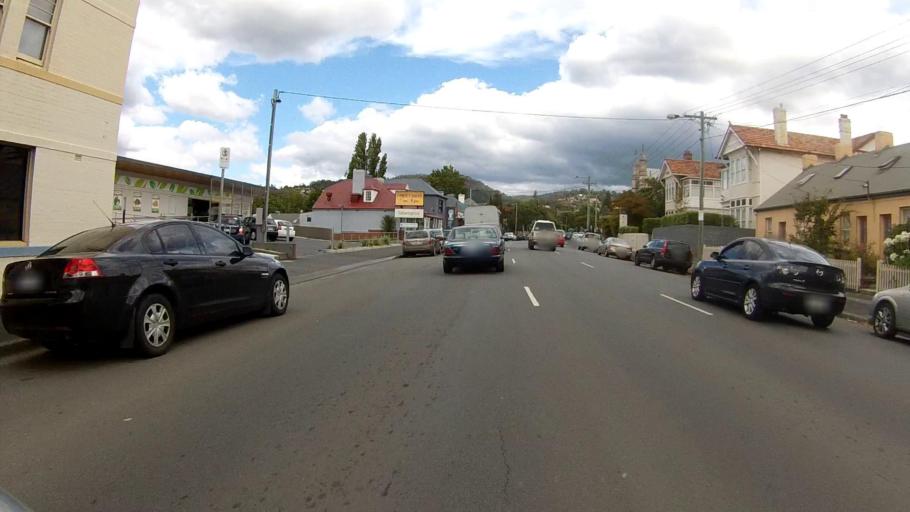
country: AU
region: Tasmania
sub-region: Hobart
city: Sandy Bay
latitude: -42.8917
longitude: 147.3204
